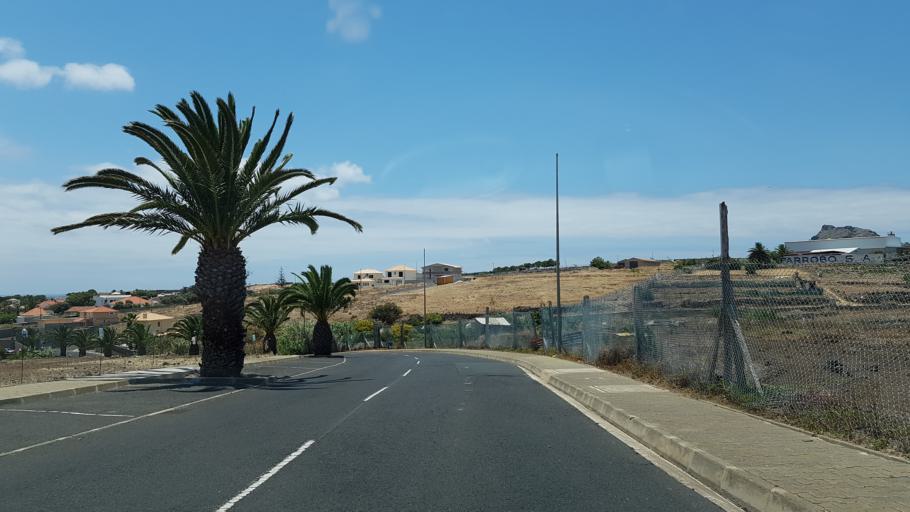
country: PT
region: Madeira
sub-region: Porto Santo
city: Vila de Porto Santo
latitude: 33.0632
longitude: -16.3439
